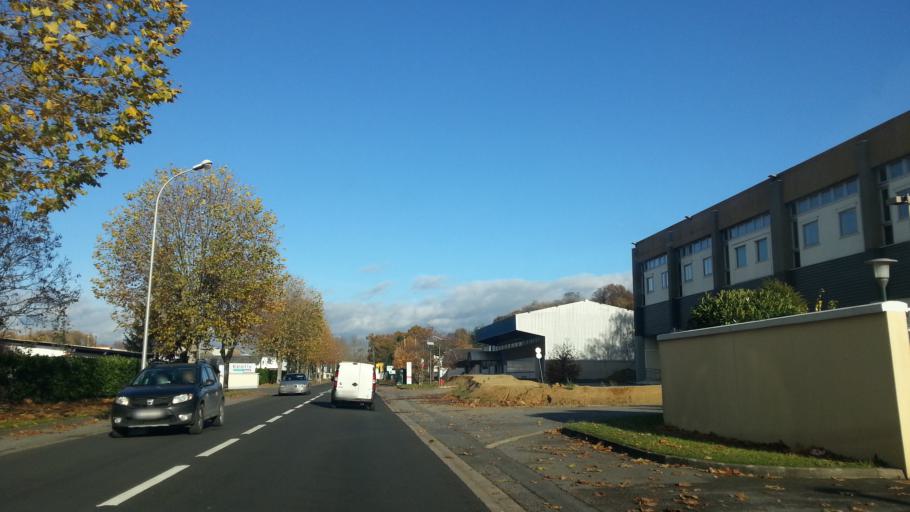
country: FR
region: Picardie
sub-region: Departement de l'Oise
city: Creil
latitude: 49.2710
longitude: 2.4954
